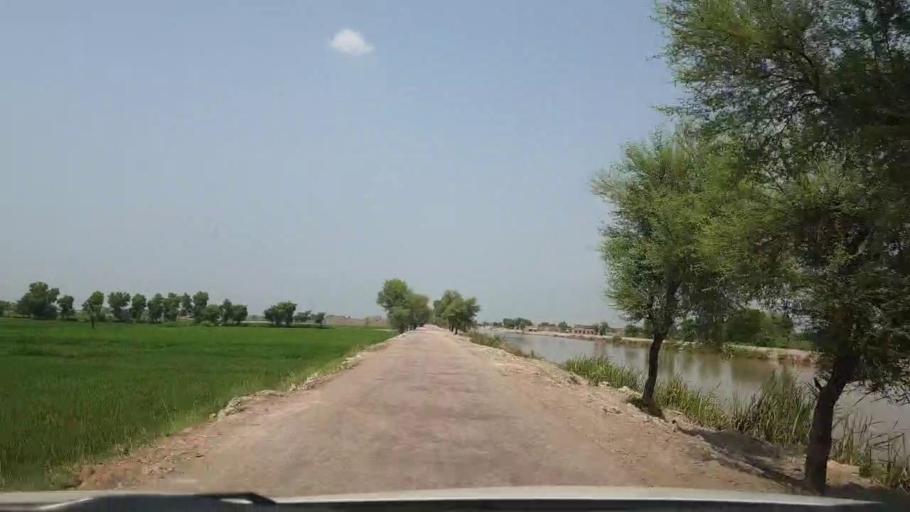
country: PK
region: Sindh
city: Dokri
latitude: 27.3321
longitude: 68.1097
